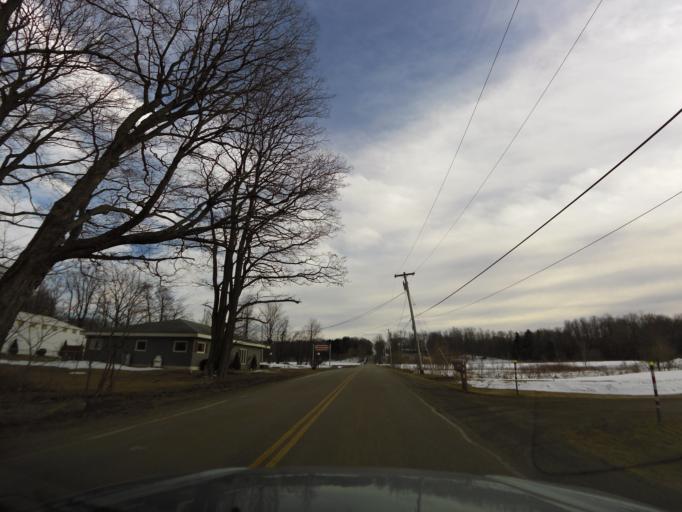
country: US
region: New York
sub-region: Cattaraugus County
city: Delevan
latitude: 42.4966
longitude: -78.5091
